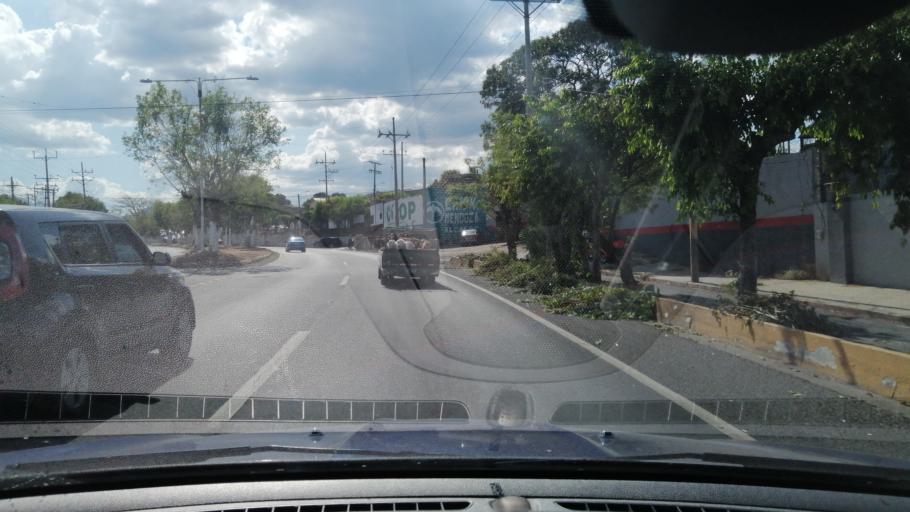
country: SV
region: Santa Ana
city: Santa Ana
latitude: 13.9853
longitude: -89.5509
